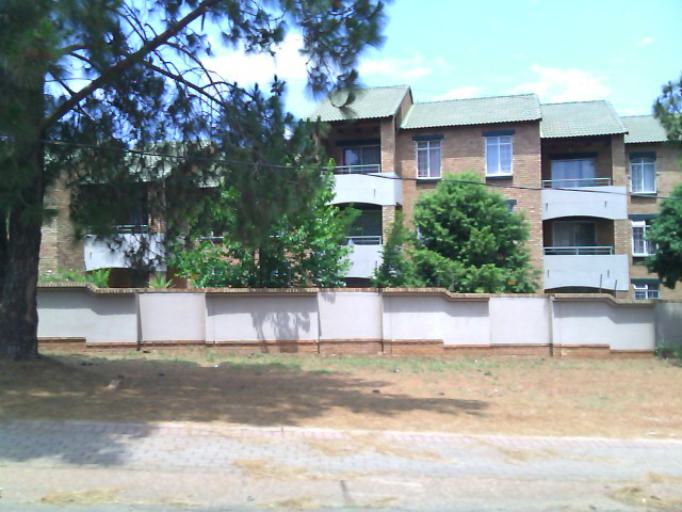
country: ZA
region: Gauteng
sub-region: City of Tshwane Metropolitan Municipality
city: Centurion
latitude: -25.8437
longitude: 28.1947
